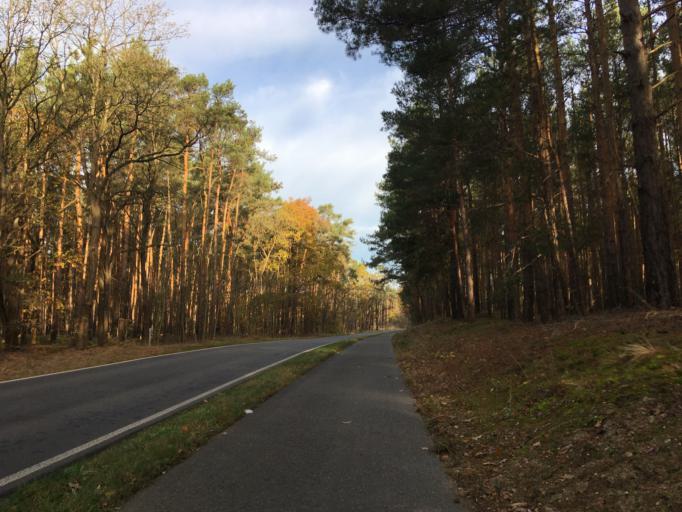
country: DE
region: Brandenburg
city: Luebben
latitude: 51.9552
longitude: 13.8818
